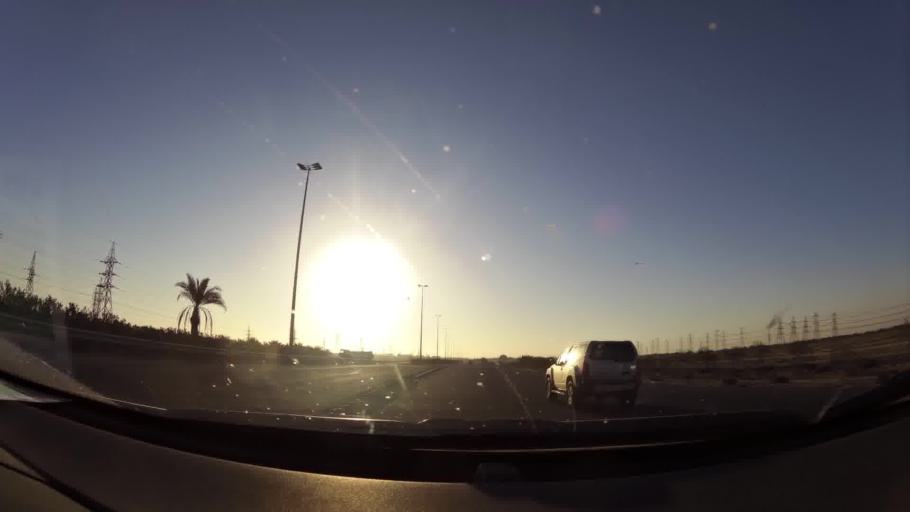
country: KW
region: Al Ahmadi
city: Al Fahahil
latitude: 28.9319
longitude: 48.1951
